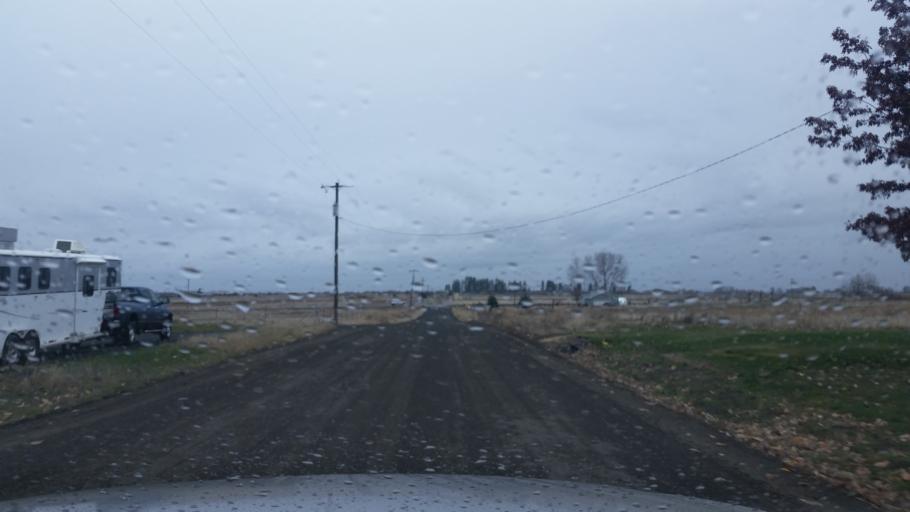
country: US
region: Washington
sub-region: Spokane County
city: Fairchild Air Force Base
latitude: 47.5882
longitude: -117.6289
